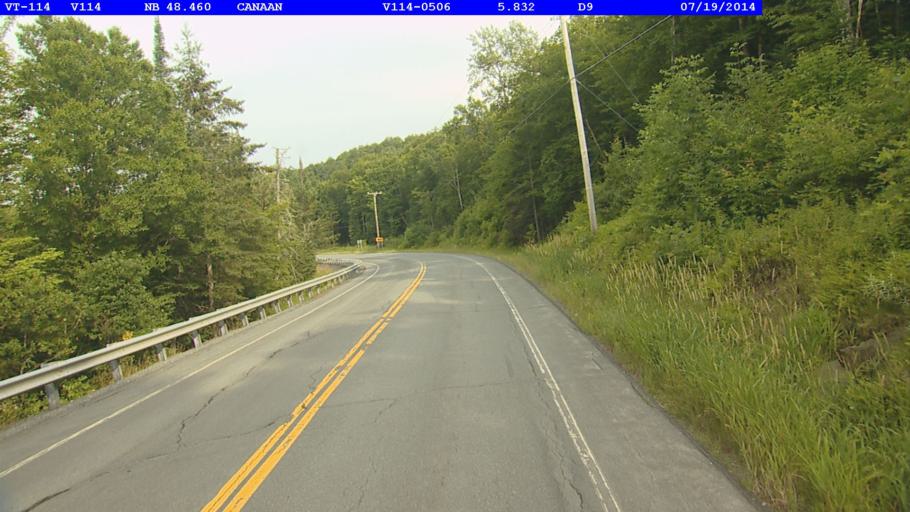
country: US
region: New Hampshire
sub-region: Coos County
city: Colebrook
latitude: 45.0091
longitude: -71.5791
